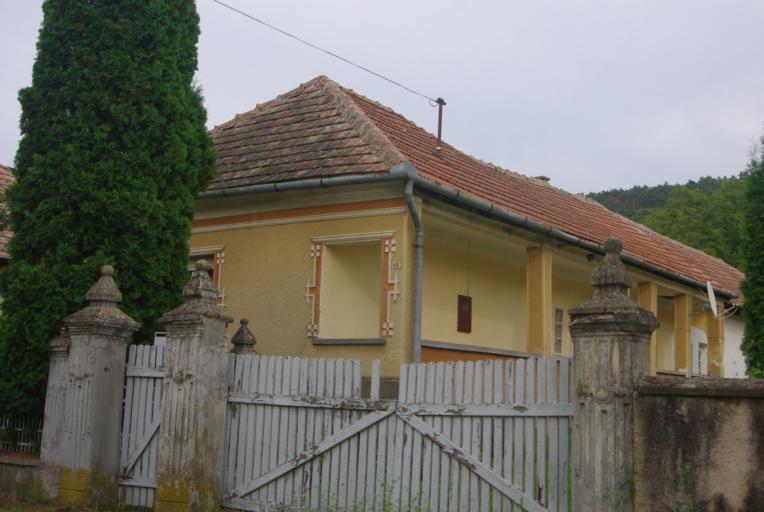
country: HU
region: Borsod-Abauj-Zemplen
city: Gonc
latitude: 48.3888
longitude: 21.2842
